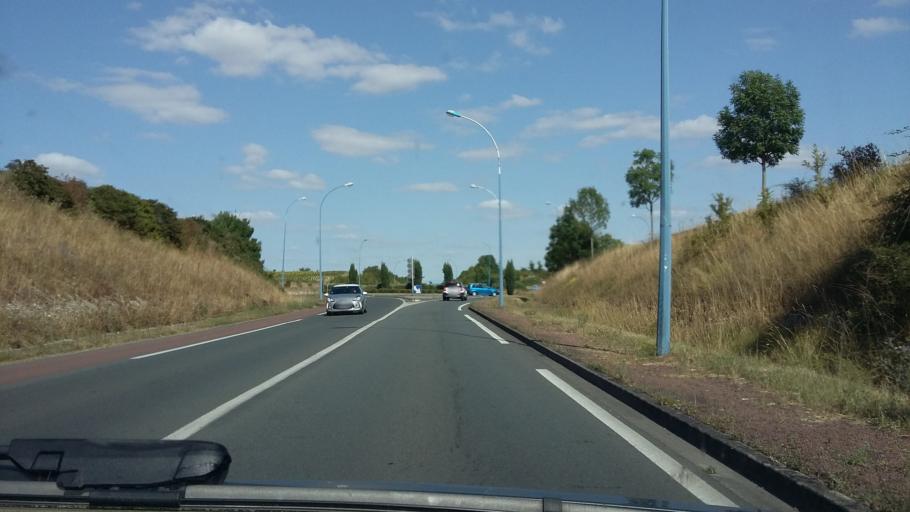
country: FR
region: Poitou-Charentes
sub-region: Departement de la Charente-Maritime
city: Saint-Jean-d'Angely
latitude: 45.9564
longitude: -0.5304
